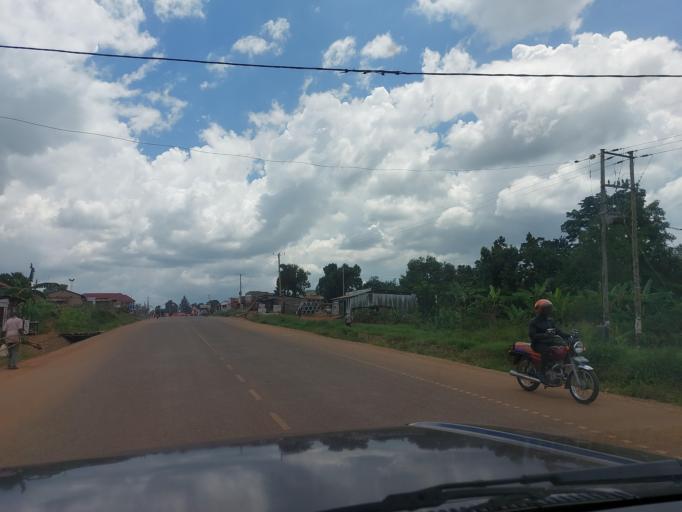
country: UG
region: Central Region
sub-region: Mukono District
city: Mukono
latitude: 0.3195
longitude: 32.7672
